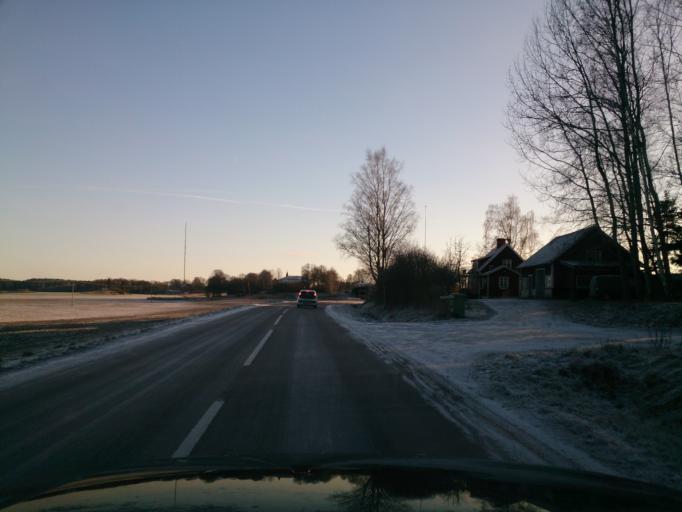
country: SE
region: OEstergoetland
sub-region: Norrkopings Kommun
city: Kimstad
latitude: 58.4156
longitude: 15.9193
